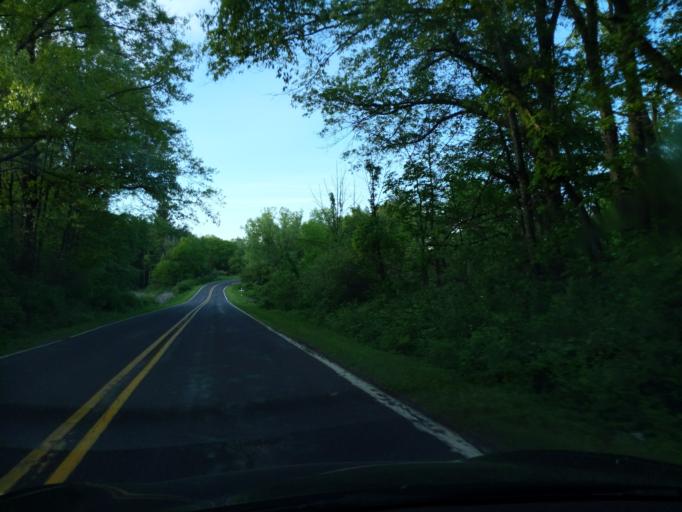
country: US
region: Michigan
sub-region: Ingham County
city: Leslie
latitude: 42.5073
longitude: -84.3121
